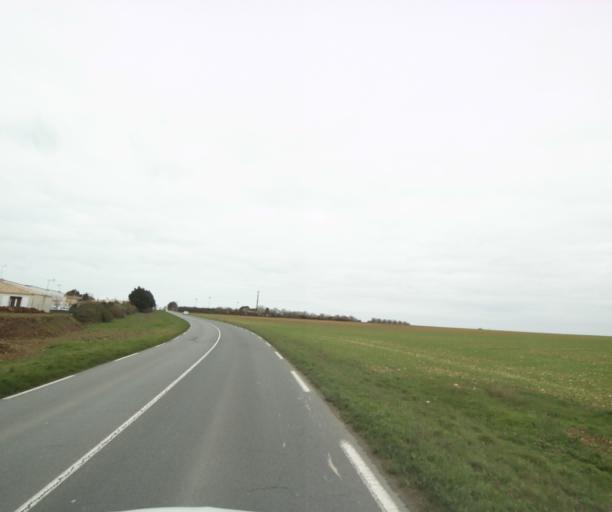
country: FR
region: Poitou-Charentes
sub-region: Departement de la Charente-Maritime
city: Lagord
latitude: 46.1929
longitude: -1.1486
